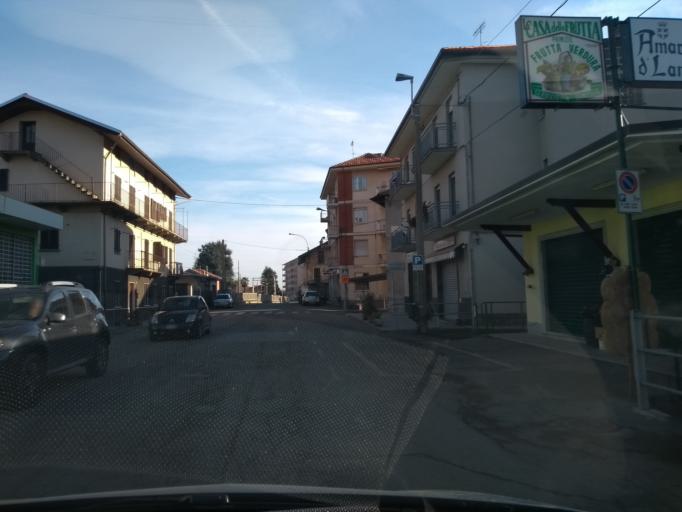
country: IT
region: Piedmont
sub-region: Provincia di Torino
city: Lanzo Torinese
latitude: 45.2729
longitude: 7.4834
